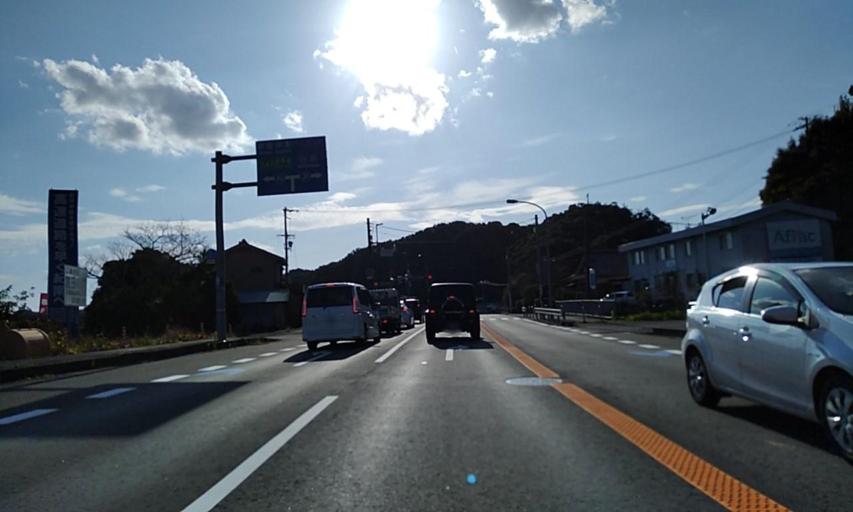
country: JP
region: Wakayama
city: Tanabe
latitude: 33.6810
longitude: 135.4081
